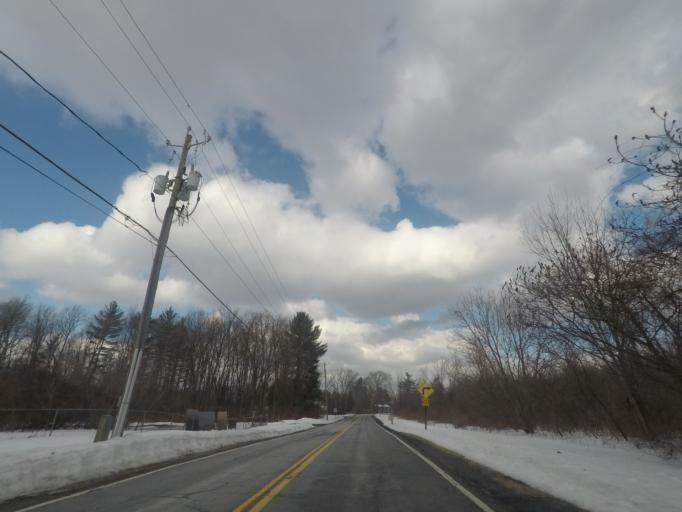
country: US
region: New York
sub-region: Saratoga County
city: Country Knolls
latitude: 42.9146
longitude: -73.7719
